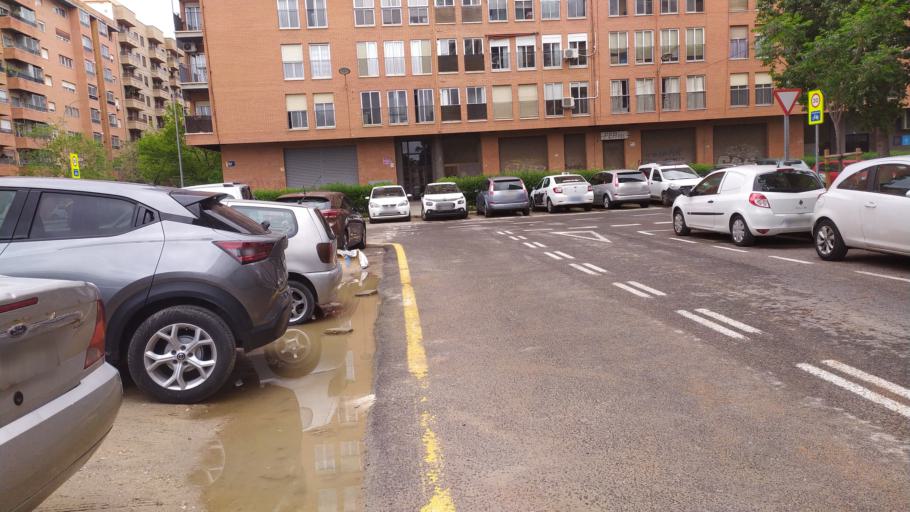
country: ES
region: Valencia
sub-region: Provincia de Valencia
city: Mislata
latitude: 39.4690
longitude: -0.4108
